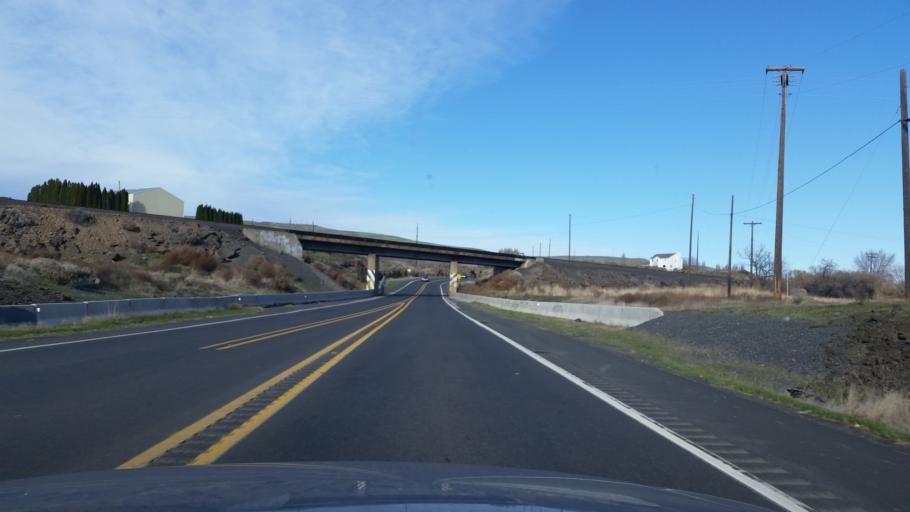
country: US
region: Washington
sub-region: Grant County
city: Ephrata
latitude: 47.2768
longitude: -119.5799
